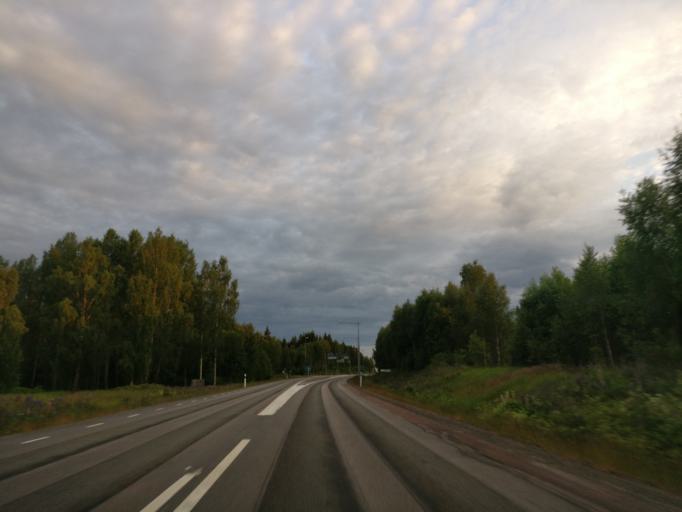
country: SE
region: Vaermland
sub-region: Hagfors Kommun
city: Hagfors
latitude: 59.9962
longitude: 13.5999
